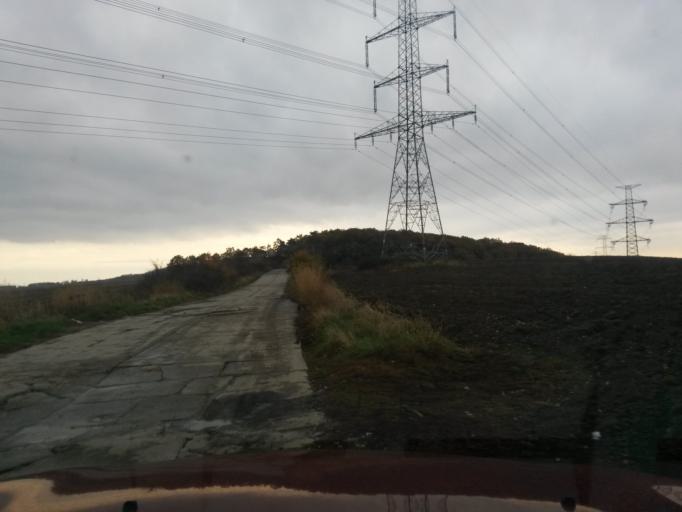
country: SK
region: Kosicky
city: Kosice
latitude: 48.8038
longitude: 21.2745
